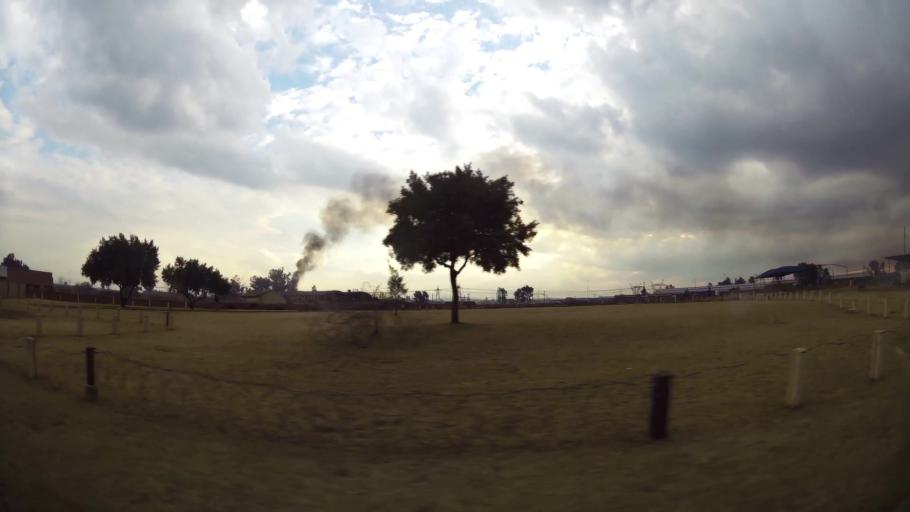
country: ZA
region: Gauteng
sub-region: Ekurhuleni Metropolitan Municipality
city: Germiston
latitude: -26.3554
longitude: 28.1254
